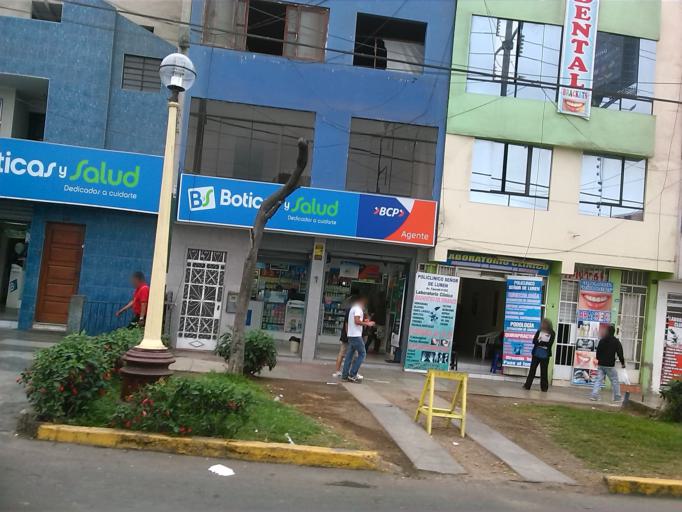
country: PE
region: Callao
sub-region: Callao
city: Callao
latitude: -12.0432
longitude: -77.0984
